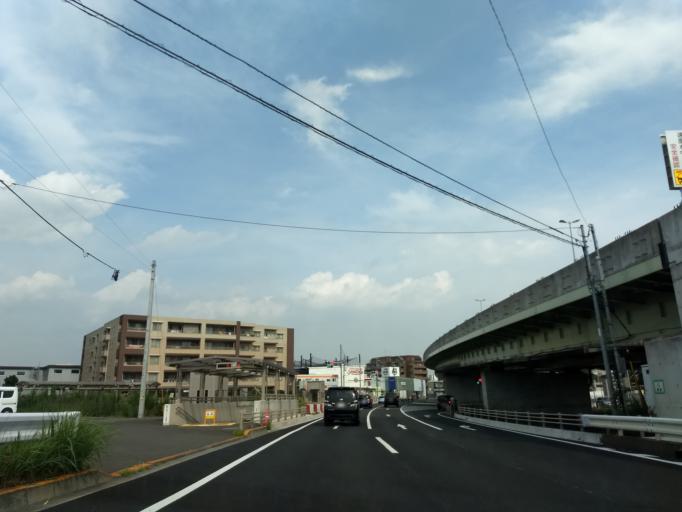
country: JP
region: Tokyo
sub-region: Machida-shi
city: Machida
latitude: 35.5132
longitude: 139.4698
